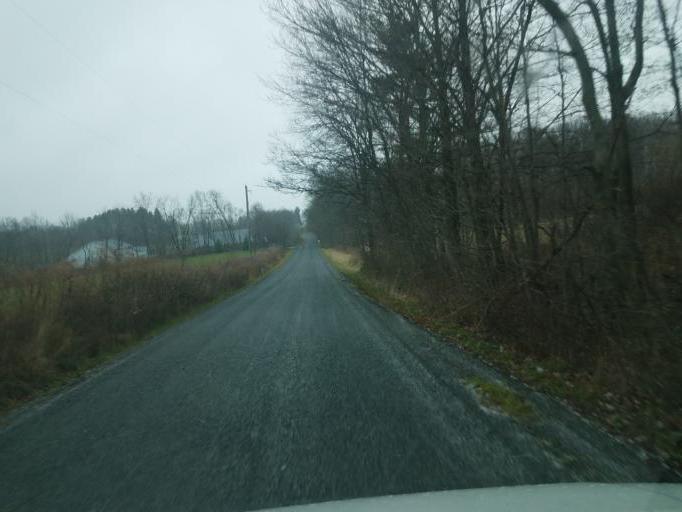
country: US
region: Ohio
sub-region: Morrow County
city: Mount Gilead
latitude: 40.5566
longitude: -82.7008
